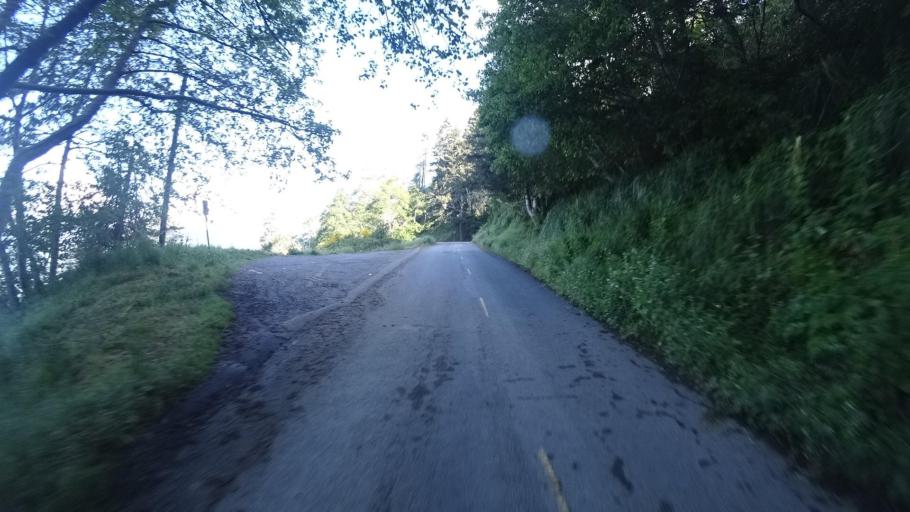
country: US
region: California
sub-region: Humboldt County
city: Westhaven-Moonstone
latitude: 41.0490
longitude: -124.1244
